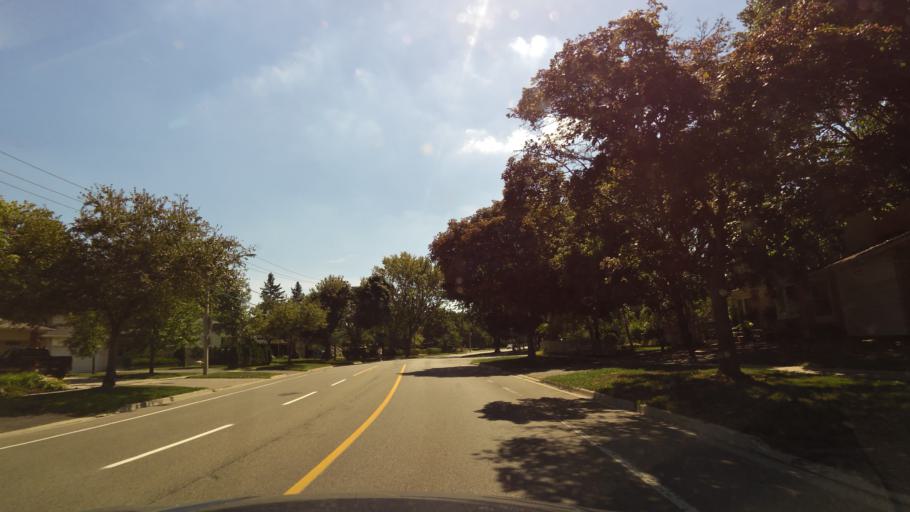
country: CA
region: Ontario
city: Mississauga
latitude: 43.5258
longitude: -79.6363
